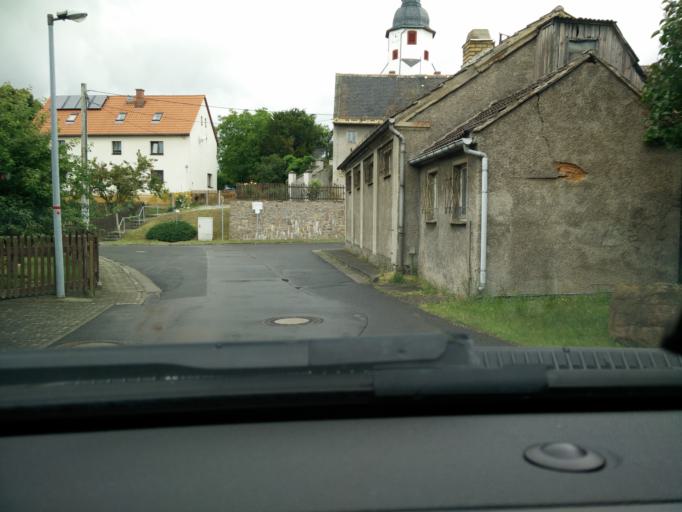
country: DE
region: Saxony
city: Bad Lausick
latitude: 51.1362
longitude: 12.6919
